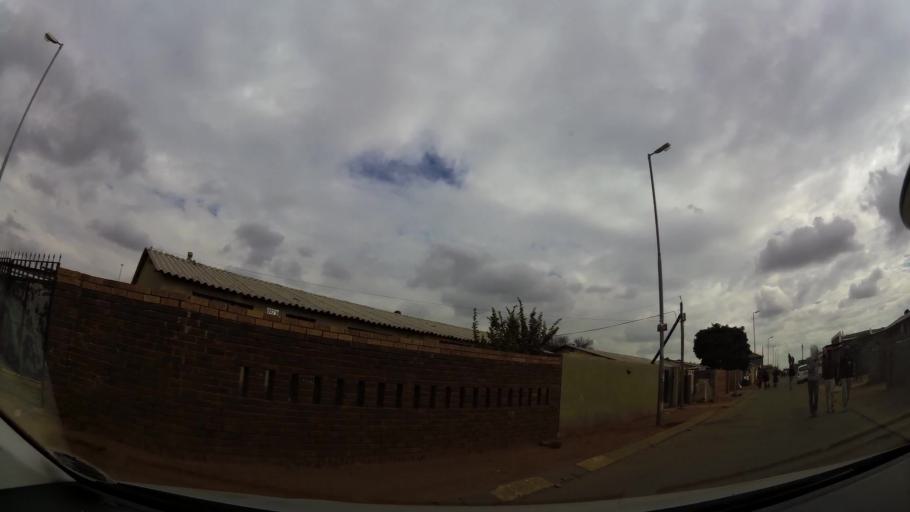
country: ZA
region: Gauteng
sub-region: City of Johannesburg Metropolitan Municipality
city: Soweto
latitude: -26.2764
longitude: 27.8576
